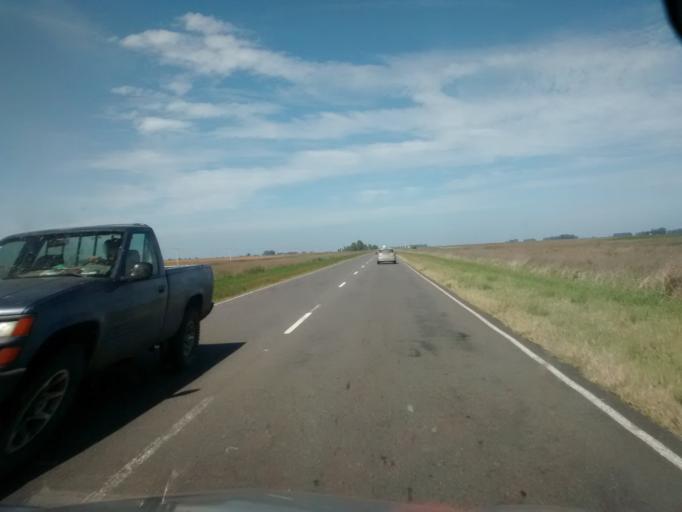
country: AR
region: Buenos Aires
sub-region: Partido de Ayacucho
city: Ayacucho
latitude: -36.6753
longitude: -58.5749
